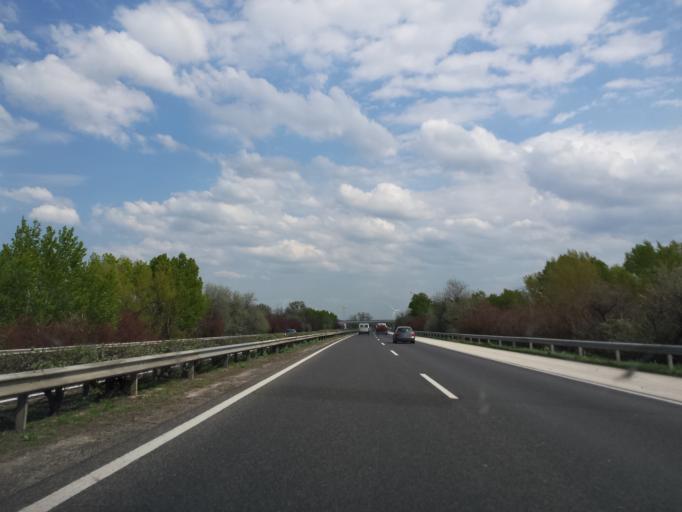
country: HU
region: Komarom-Esztergom
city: Acs
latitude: 47.6817
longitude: 18.0265
